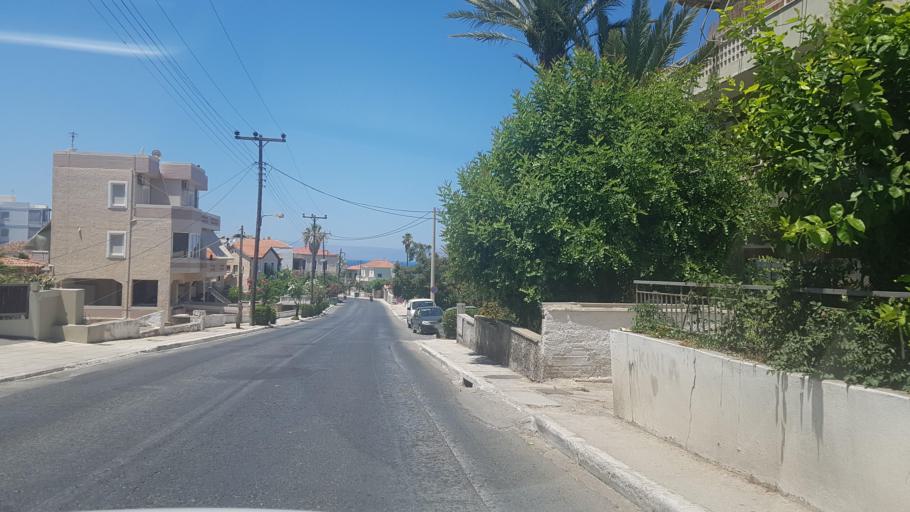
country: GR
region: Crete
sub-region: Nomos Chanias
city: Chania
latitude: 35.5160
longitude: 24.0351
